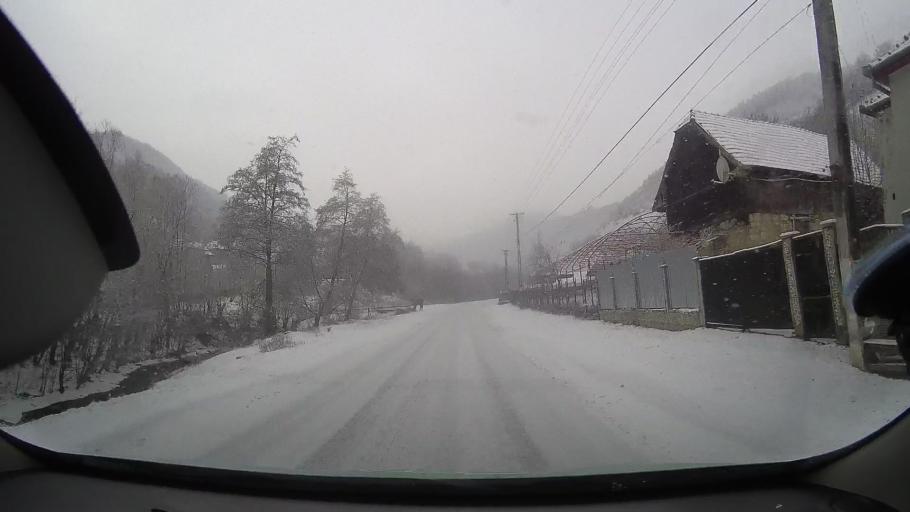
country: RO
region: Cluj
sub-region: Comuna Moldovenesti
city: Moldovenesti
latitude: 46.5039
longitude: 23.5986
